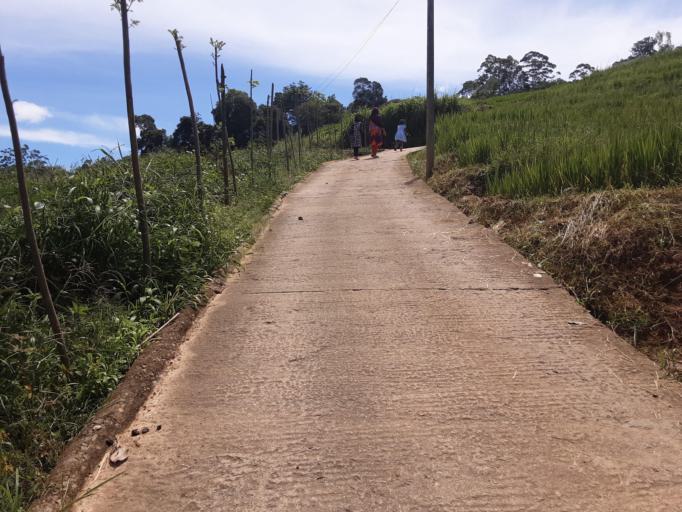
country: LK
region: Uva
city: Haputale
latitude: 6.8935
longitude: 80.9260
